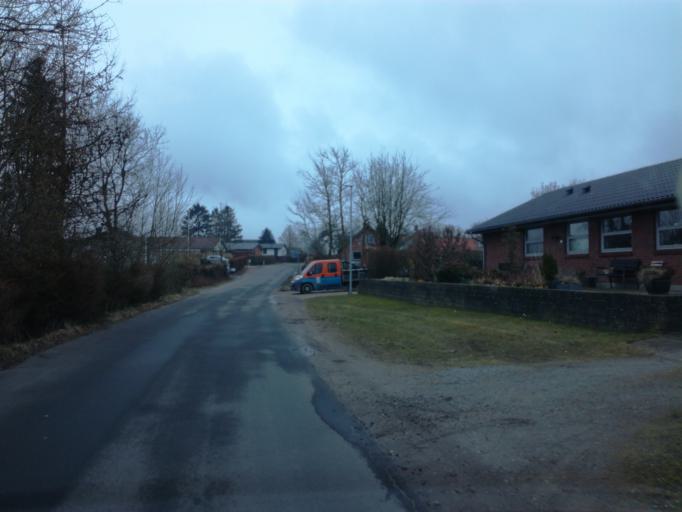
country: DK
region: South Denmark
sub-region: Vejle Kommune
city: Borkop
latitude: 55.6402
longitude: 9.5967
